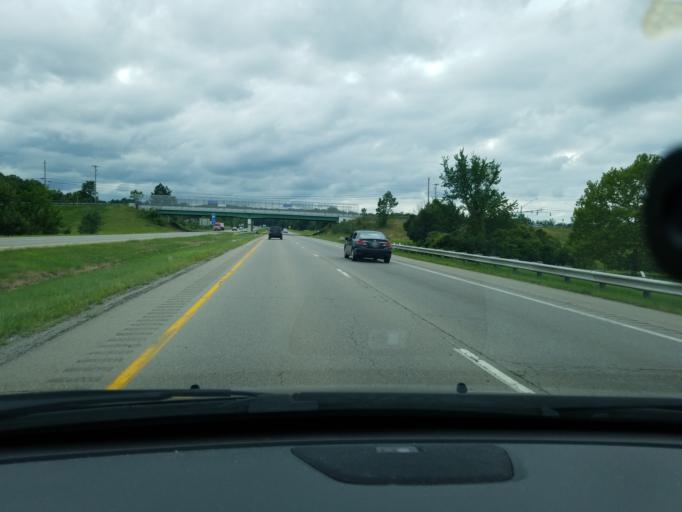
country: US
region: Ohio
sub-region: Lorain County
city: Amherst
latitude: 41.4109
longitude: -82.2370
